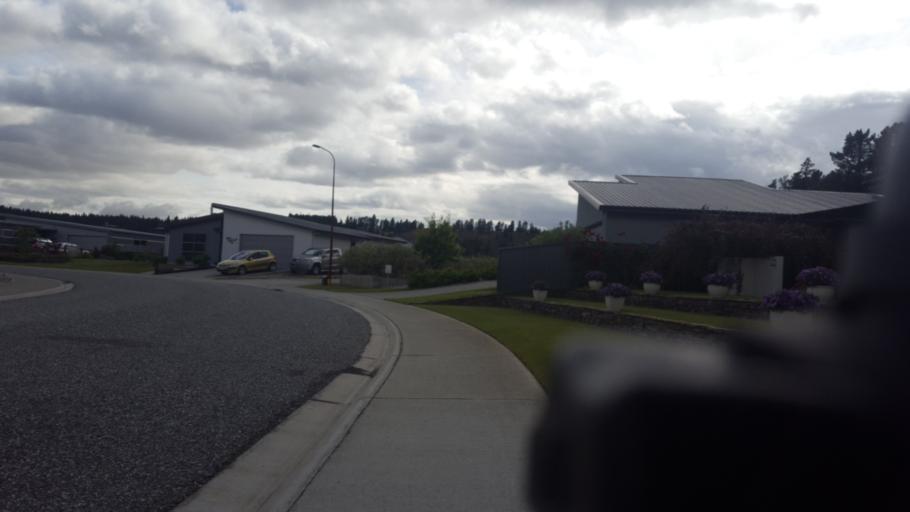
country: NZ
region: Otago
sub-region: Queenstown-Lakes District
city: Wanaka
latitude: -45.2403
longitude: 169.3820
